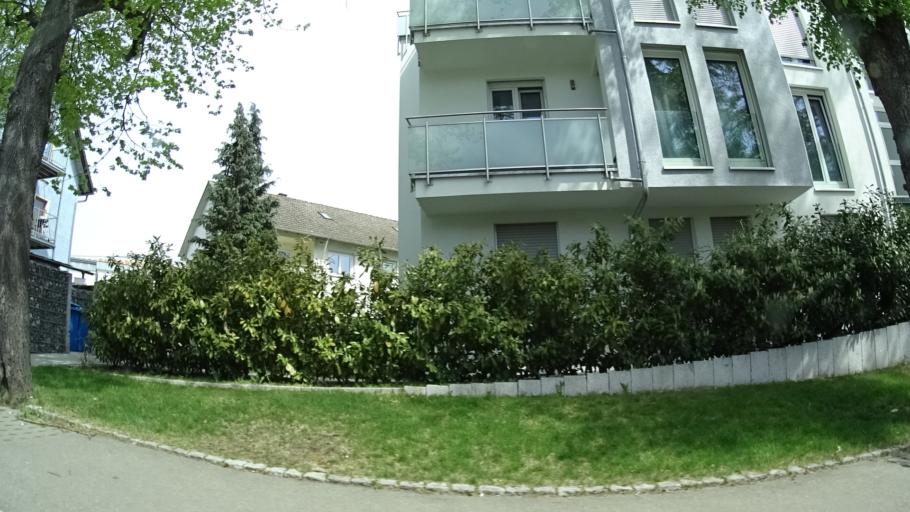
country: DE
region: Baden-Wuerttemberg
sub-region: Freiburg Region
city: Rottweil
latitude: 48.1601
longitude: 8.6407
